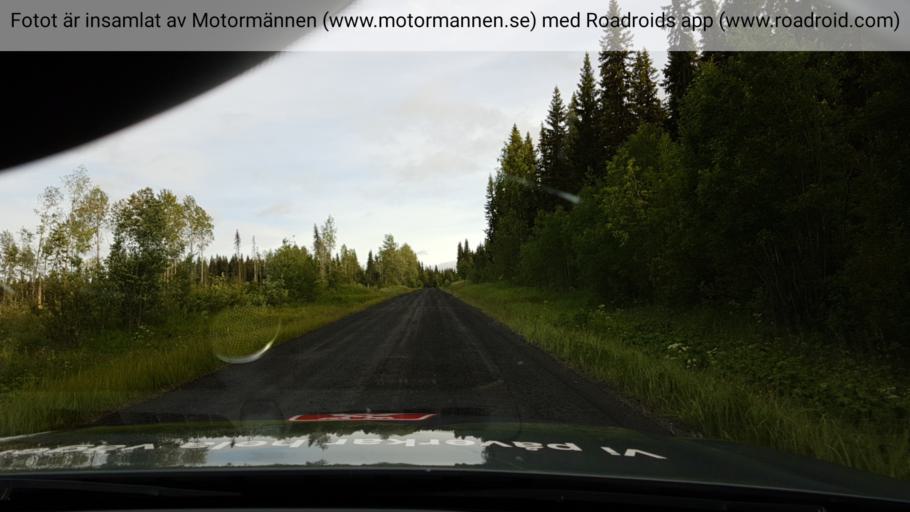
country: SE
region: Jaemtland
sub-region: OEstersunds Kommun
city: Lit
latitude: 63.6483
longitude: 15.0726
